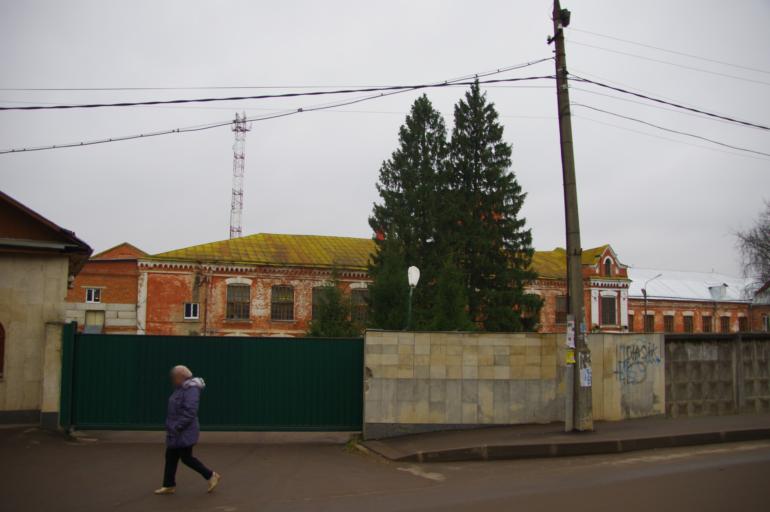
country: RU
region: Moskovskaya
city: Opalikha
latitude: 55.8416
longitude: 37.2554
